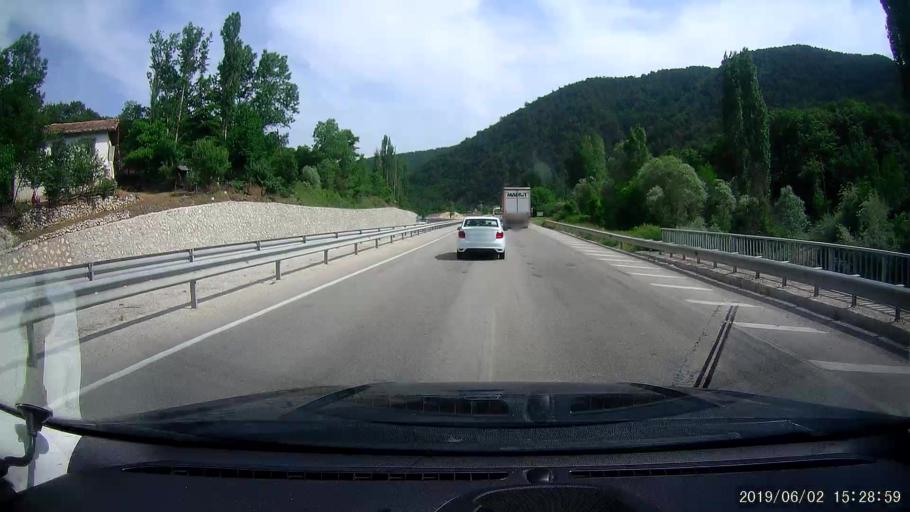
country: TR
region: Amasya
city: Saraycik
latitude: 40.9724
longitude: 35.0829
